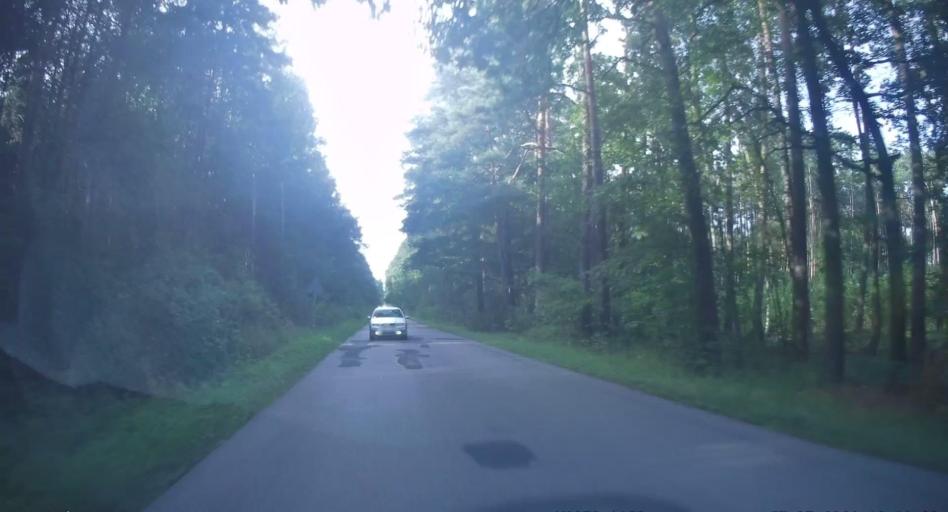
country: PL
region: Swietokrzyskie
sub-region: Powiat konecki
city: Konskie
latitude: 51.2291
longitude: 20.3833
